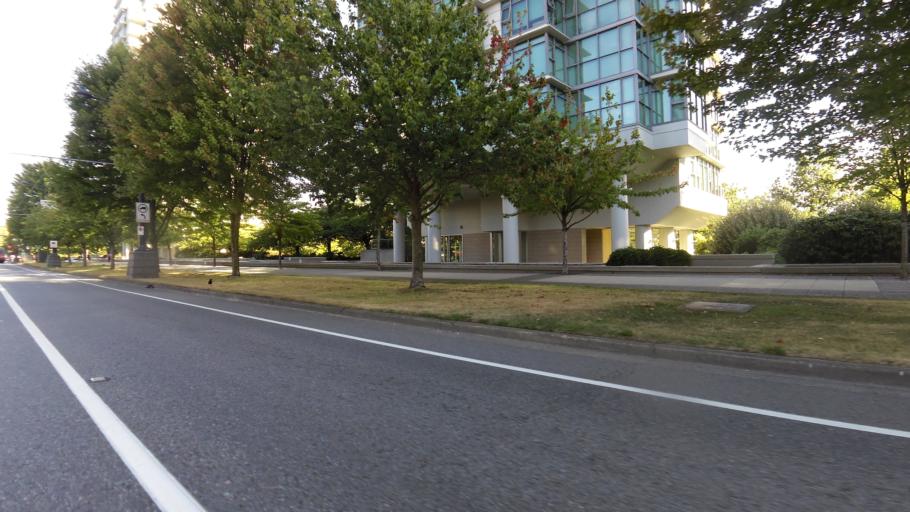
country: CA
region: British Columbia
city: West End
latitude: 49.2918
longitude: -123.1323
